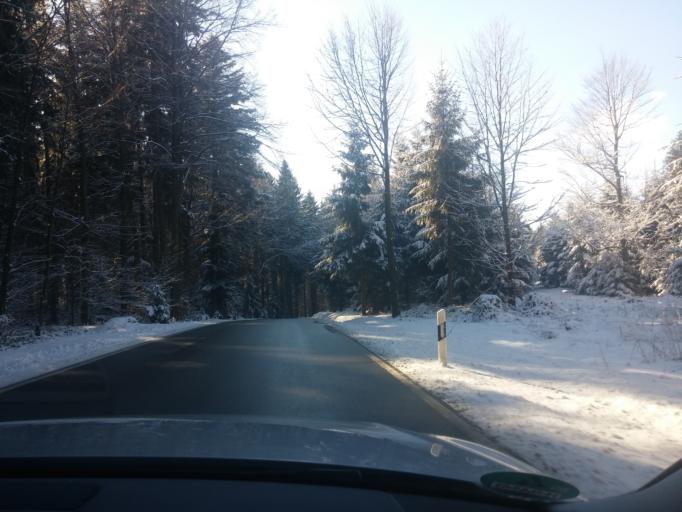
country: DE
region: Baden-Wuerttemberg
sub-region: Tuebingen Region
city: Leutkirch im Allgau
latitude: 47.8459
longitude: 10.0482
